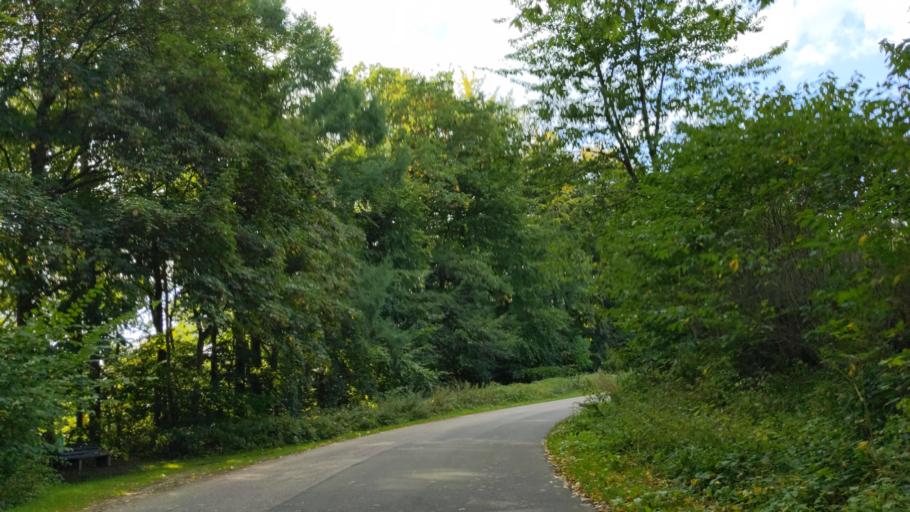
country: DE
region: Schleswig-Holstein
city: Scharbeutz
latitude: 54.0268
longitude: 10.7368
